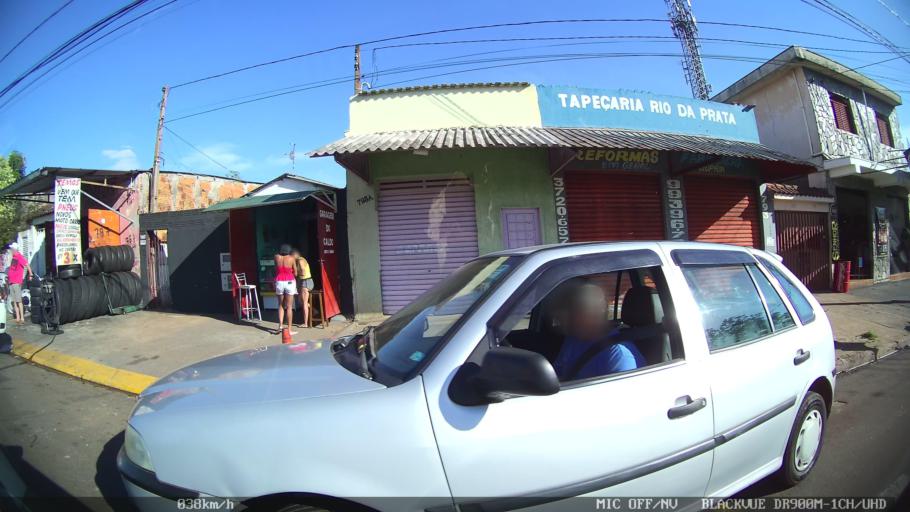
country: BR
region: Sao Paulo
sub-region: Franca
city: Franca
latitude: -20.5290
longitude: -47.4282
